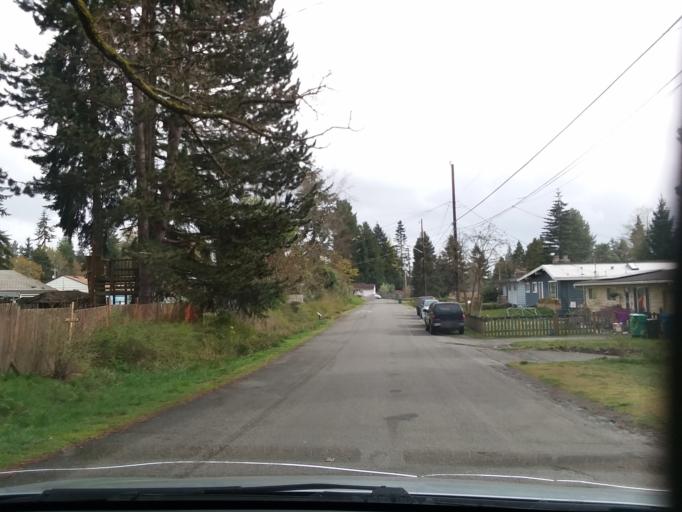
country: US
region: Washington
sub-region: King County
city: Shoreline
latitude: 47.7537
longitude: -122.3160
